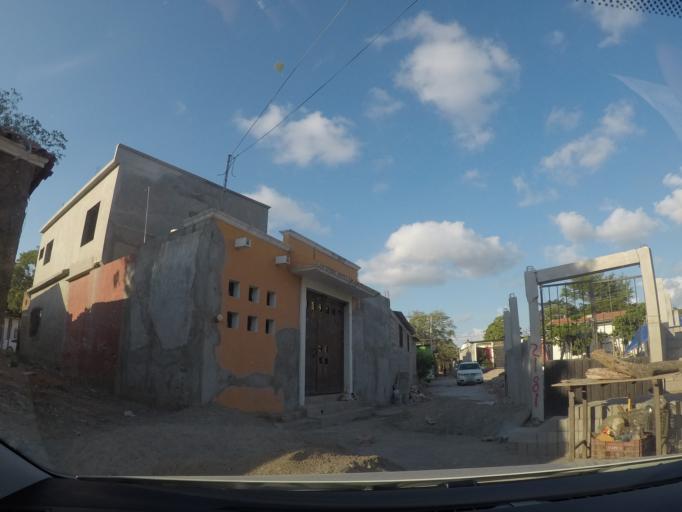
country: MX
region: Oaxaca
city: Juchitan de Zaragoza
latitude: 16.4355
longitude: -95.0282
